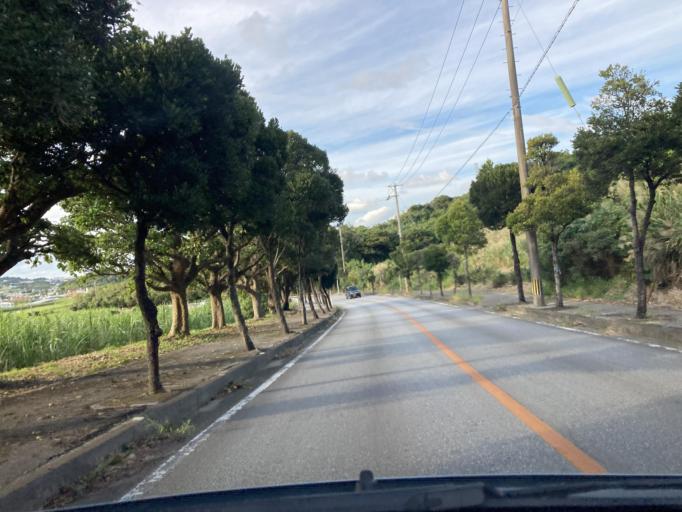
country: JP
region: Okinawa
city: Itoman
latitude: 26.1332
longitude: 127.7226
